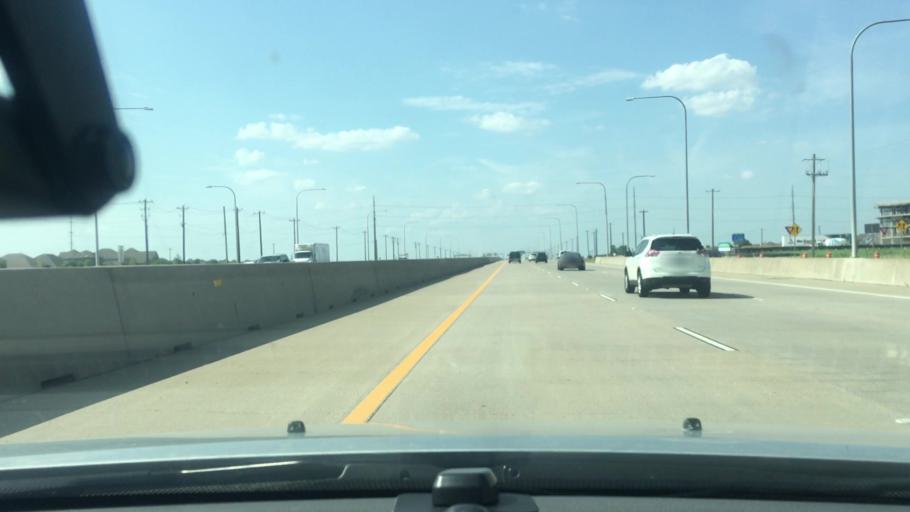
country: US
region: Texas
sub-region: Collin County
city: Frisco
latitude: 33.1785
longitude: -96.8394
